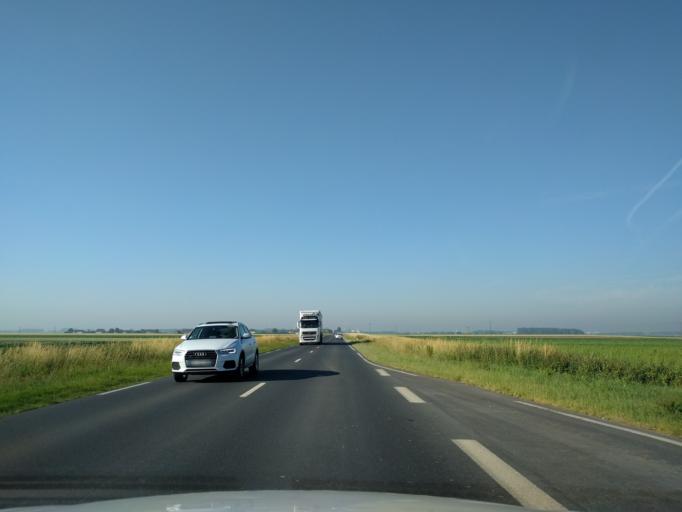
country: FR
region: Picardie
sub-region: Departement de la Somme
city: Roye
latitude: 49.7373
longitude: 2.8079
